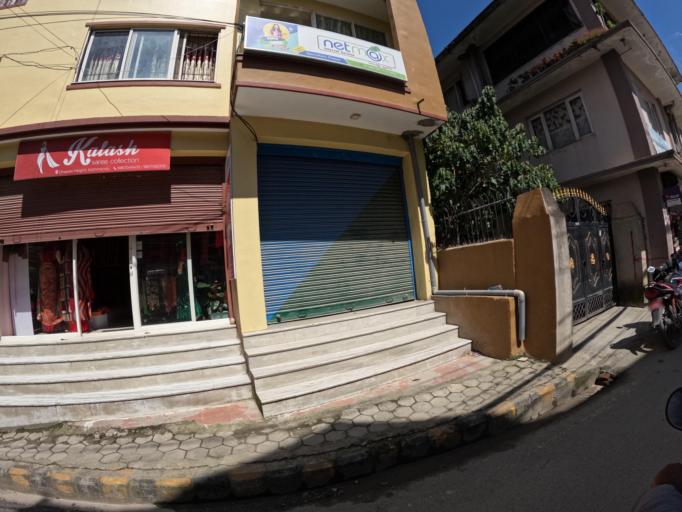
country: NP
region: Central Region
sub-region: Bagmati Zone
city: Kathmandu
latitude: 27.7461
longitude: 85.3298
